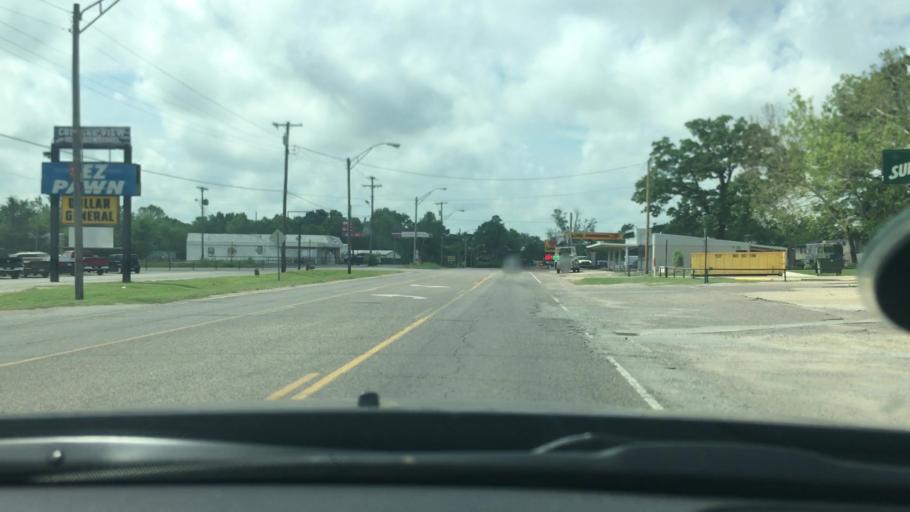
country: US
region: Oklahoma
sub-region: Bryan County
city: Durant
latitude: 34.0037
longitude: -96.3730
